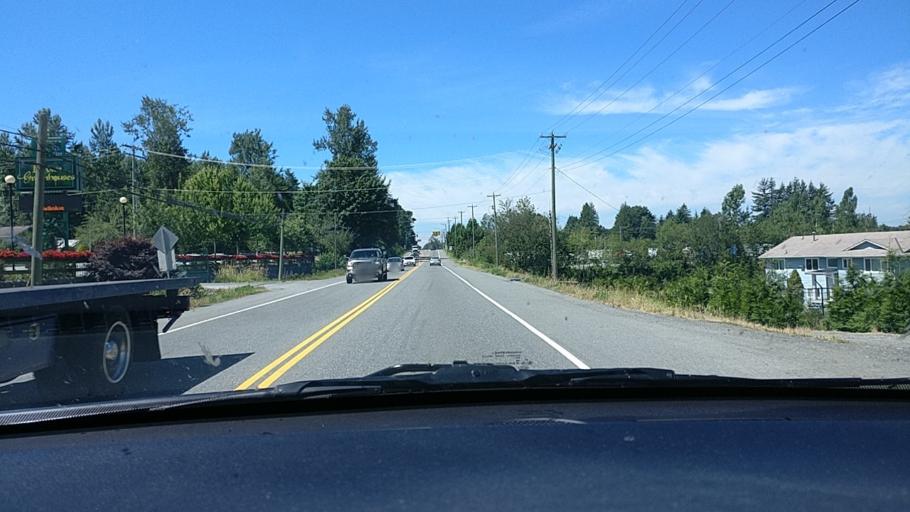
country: CA
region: British Columbia
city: Aldergrove
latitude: 49.0572
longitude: -122.4213
